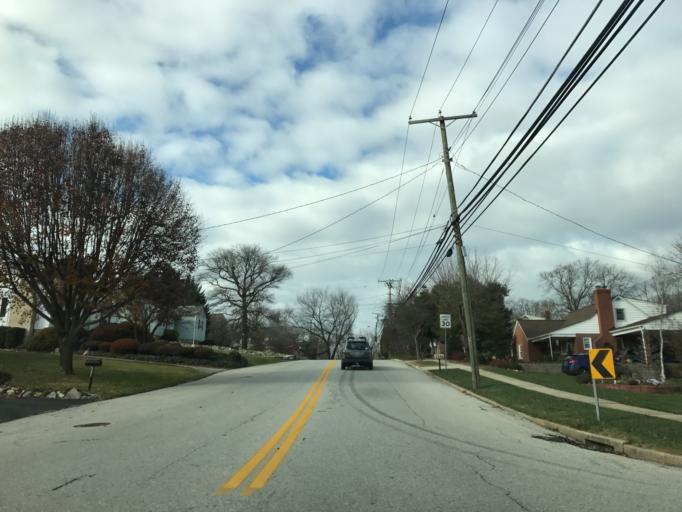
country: US
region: Maryland
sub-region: Baltimore County
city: Carney
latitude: 39.4144
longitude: -76.5171
